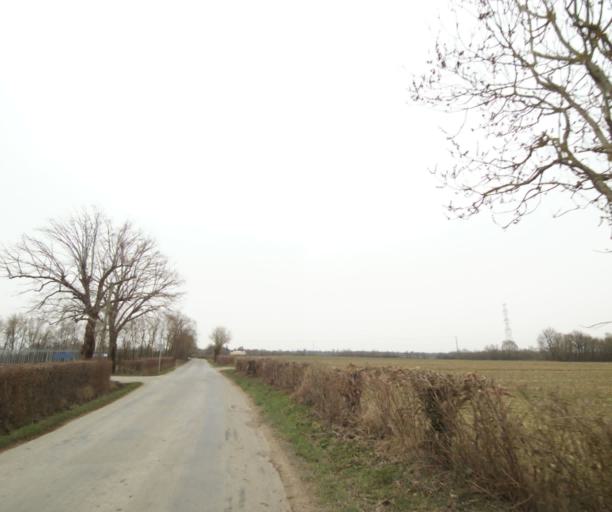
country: FR
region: Poitou-Charentes
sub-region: Departement des Deux-Sevres
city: Bessines
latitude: 46.2960
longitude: -0.4867
